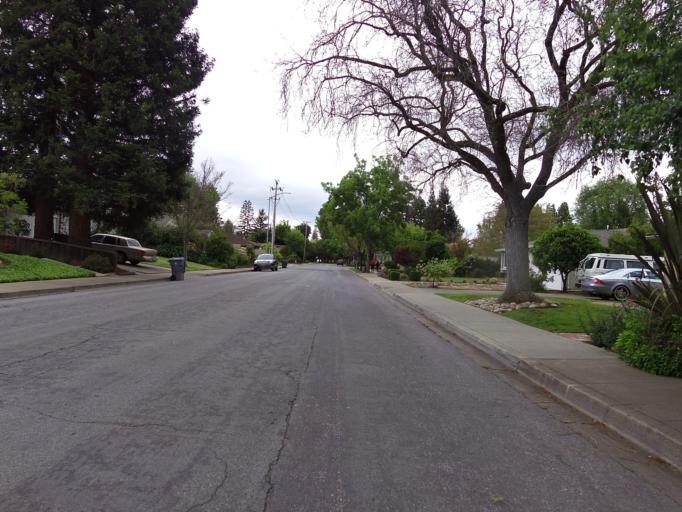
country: US
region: California
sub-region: Santa Clara County
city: Los Altos
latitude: 37.3922
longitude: -122.1006
